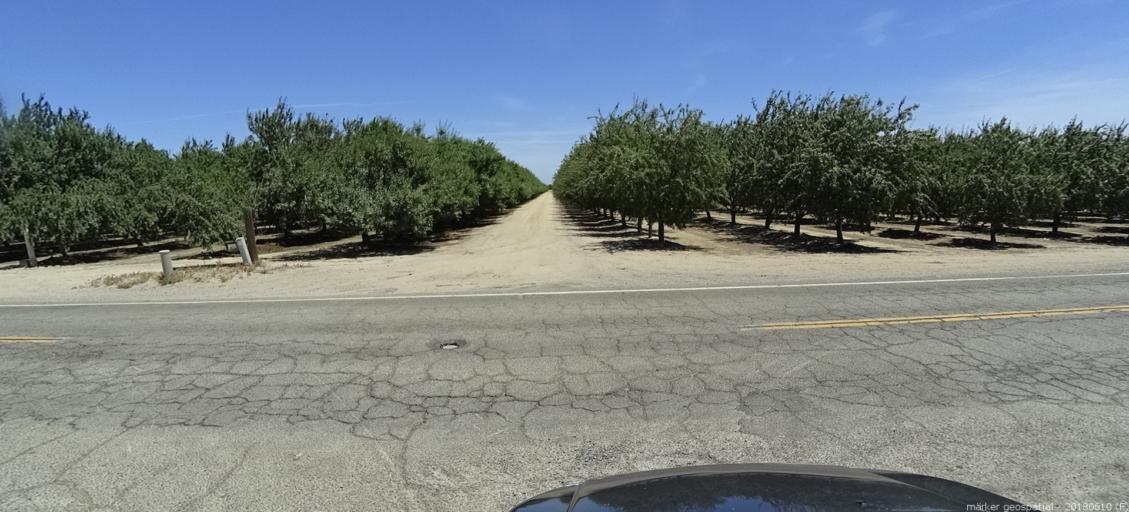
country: US
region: California
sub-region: Madera County
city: Chowchilla
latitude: 37.0765
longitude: -120.2569
